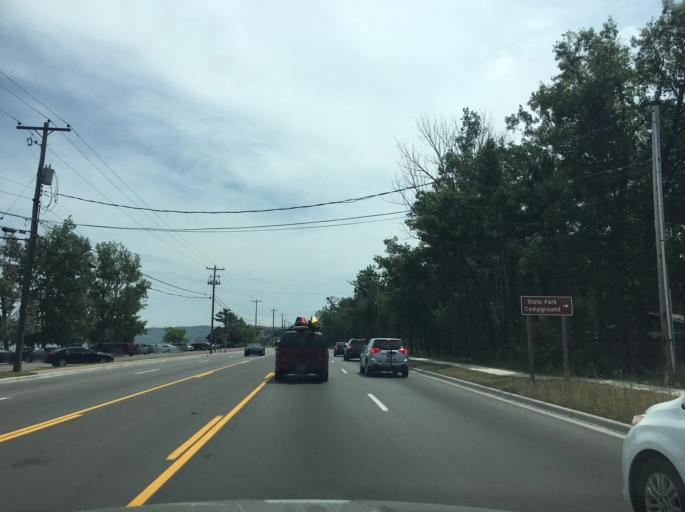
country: US
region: Michigan
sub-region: Grand Traverse County
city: Traverse City
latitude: 44.7483
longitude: -85.5549
